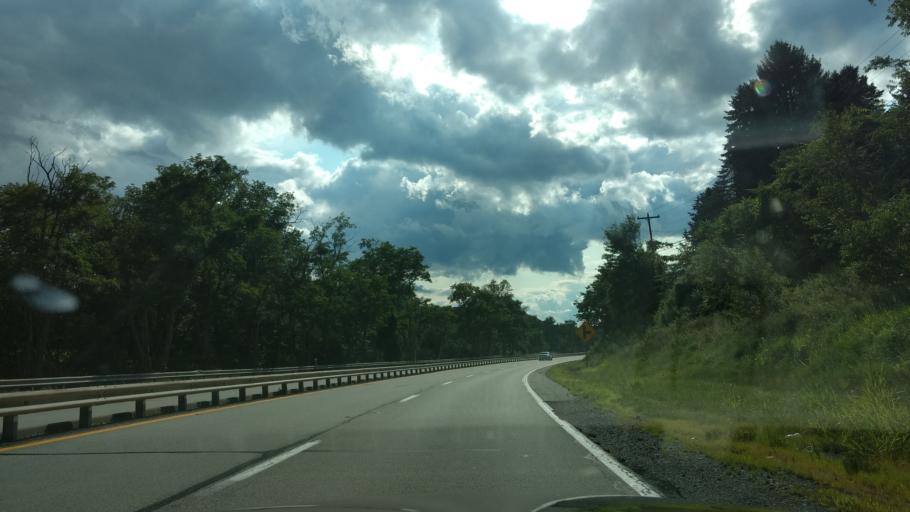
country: US
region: Pennsylvania
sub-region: Westmoreland County
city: Murrysville
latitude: 40.5116
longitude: -79.6479
